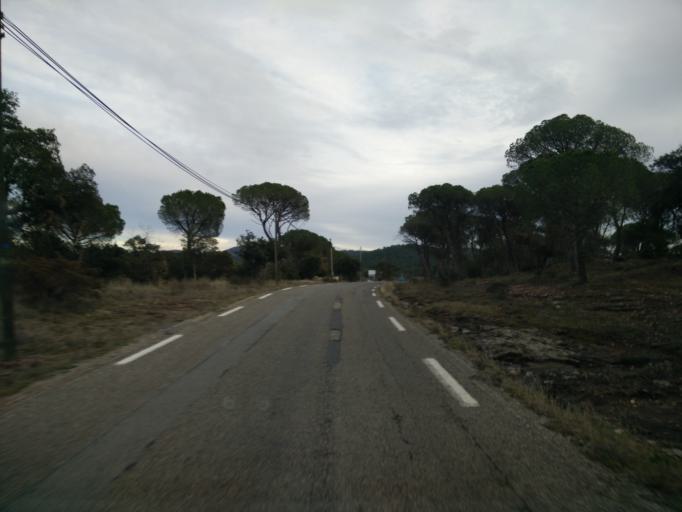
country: FR
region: Provence-Alpes-Cote d'Azur
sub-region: Departement du Var
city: Vidauban
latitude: 43.3738
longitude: 6.4470
